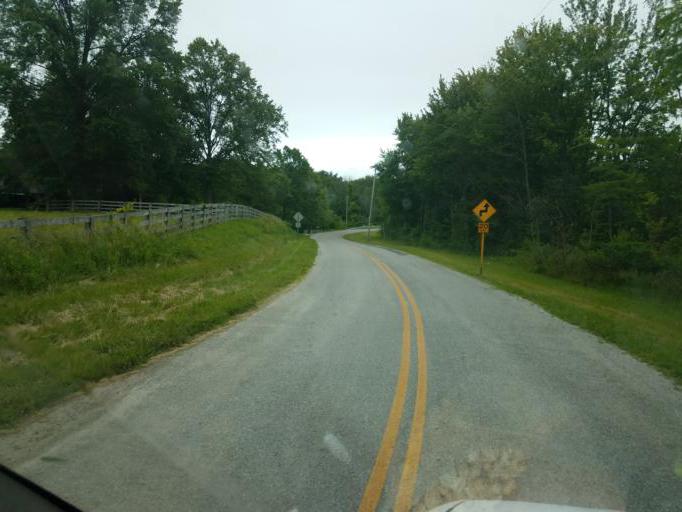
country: US
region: Ohio
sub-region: Morrow County
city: Cardington
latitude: 40.5208
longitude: -83.0145
